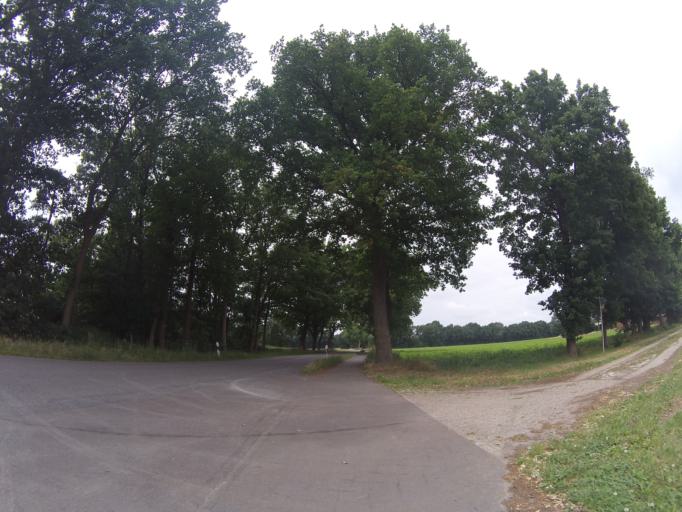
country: DE
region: Lower Saxony
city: Haren
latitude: 52.7063
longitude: 7.1826
